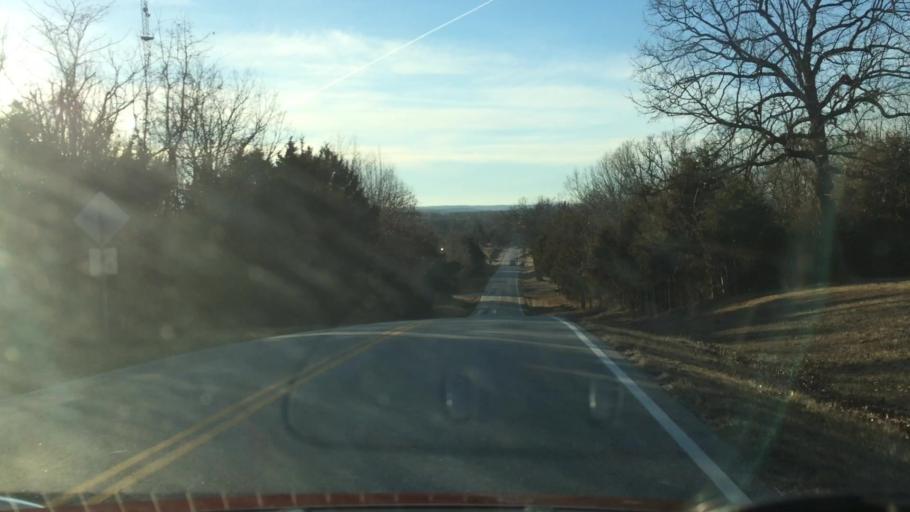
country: US
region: Missouri
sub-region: Webster County
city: Marshfield
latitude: 37.3409
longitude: -92.9782
